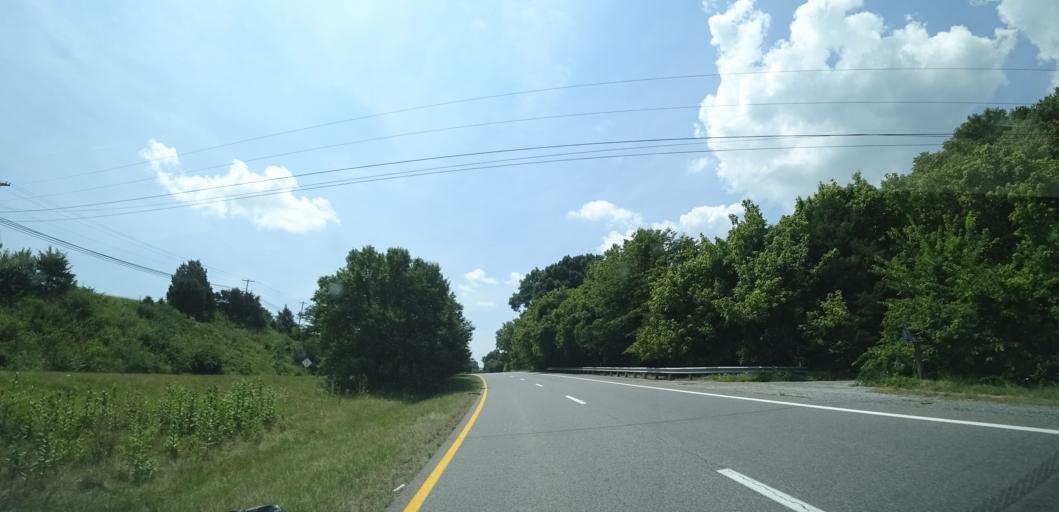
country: US
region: Virginia
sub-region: Botetourt County
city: Fincastle
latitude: 37.4867
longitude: -79.8788
